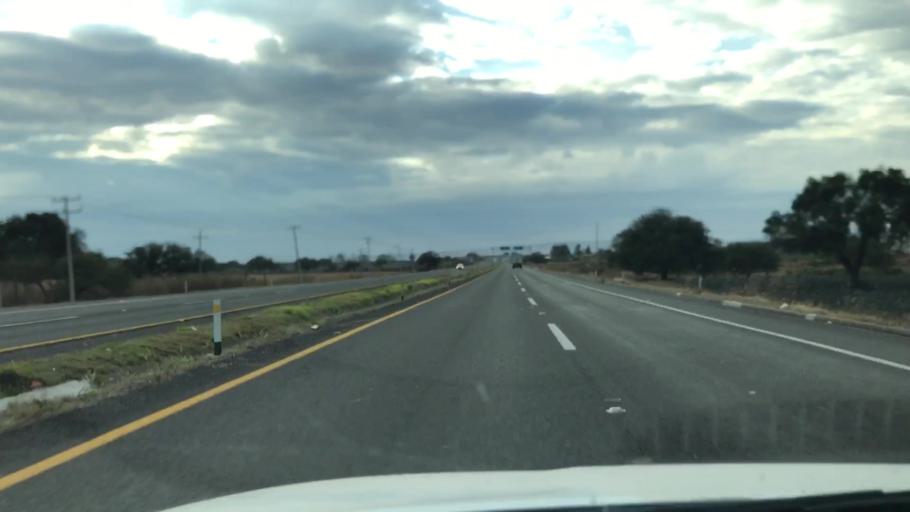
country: MX
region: Guanajuato
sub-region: Penjamo
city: Mezquite de Luna
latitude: 20.3779
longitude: -101.8517
